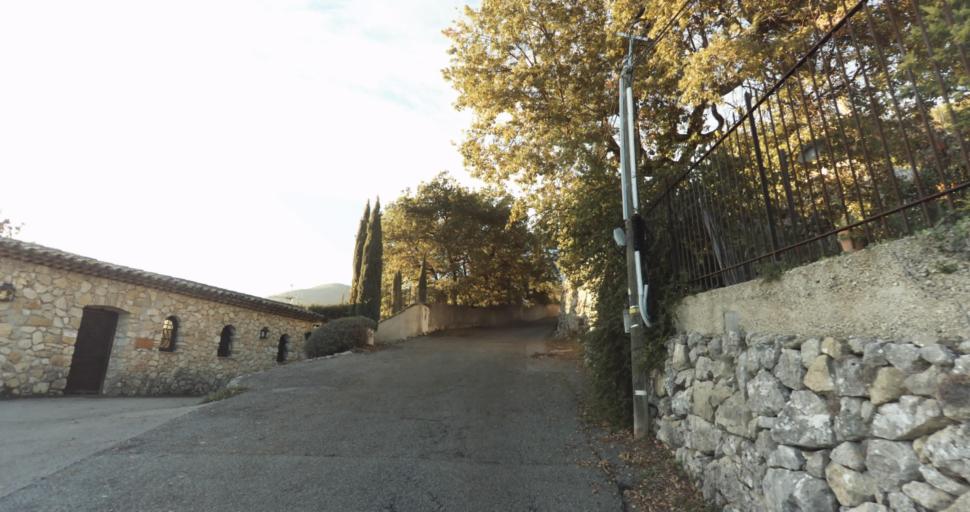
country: FR
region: Provence-Alpes-Cote d'Azur
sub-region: Departement des Alpes-Maritimes
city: Vence
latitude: 43.7337
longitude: 7.0910
